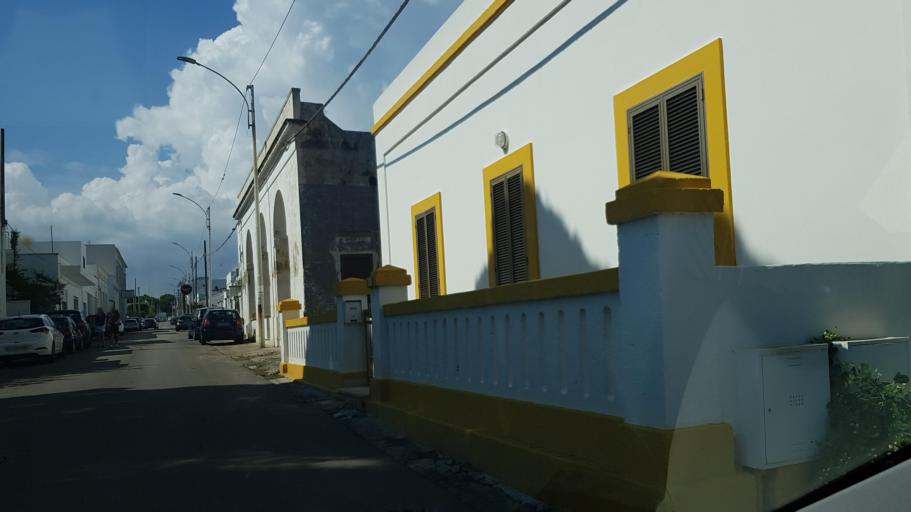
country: IT
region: Apulia
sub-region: Provincia di Lecce
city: Leuca
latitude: 39.7992
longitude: 18.3584
